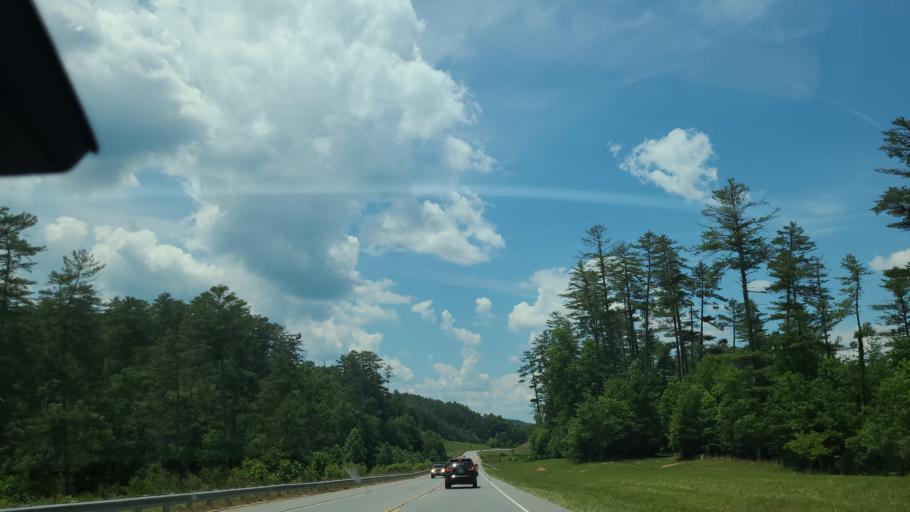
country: US
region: North Carolina
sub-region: Cherokee County
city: Murphy
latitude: 35.0713
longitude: -84.0171
